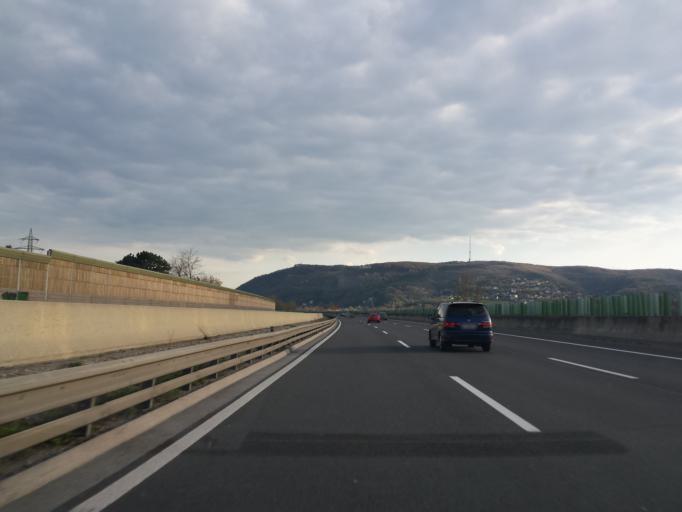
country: AT
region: Lower Austria
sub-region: Politischer Bezirk Korneuburg
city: Langenzersdorf
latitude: 48.3098
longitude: 16.3450
